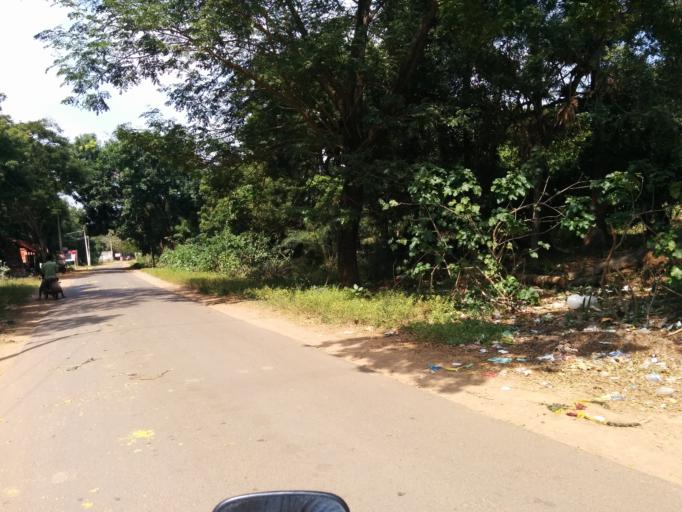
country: IN
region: Tamil Nadu
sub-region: Villupuram
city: Auroville
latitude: 11.9984
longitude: 79.8017
